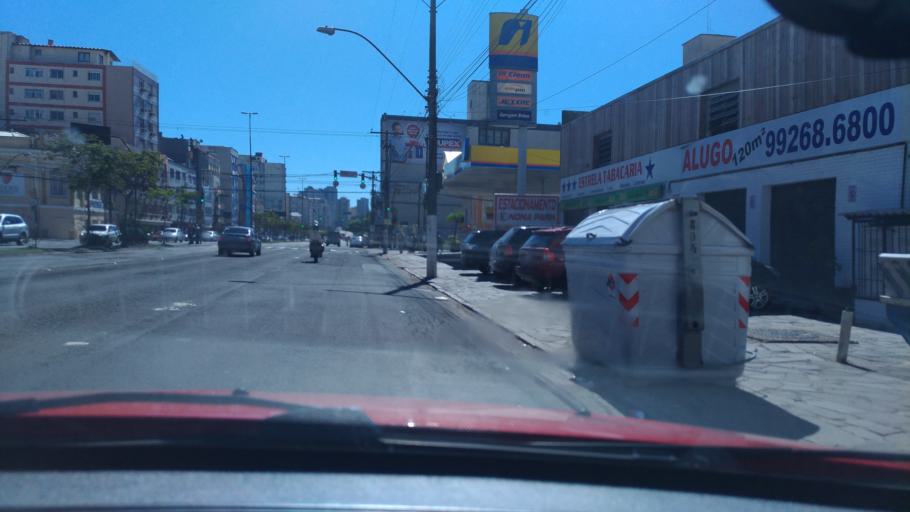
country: BR
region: Rio Grande do Sul
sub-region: Porto Alegre
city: Porto Alegre
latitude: -30.0416
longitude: -51.2159
